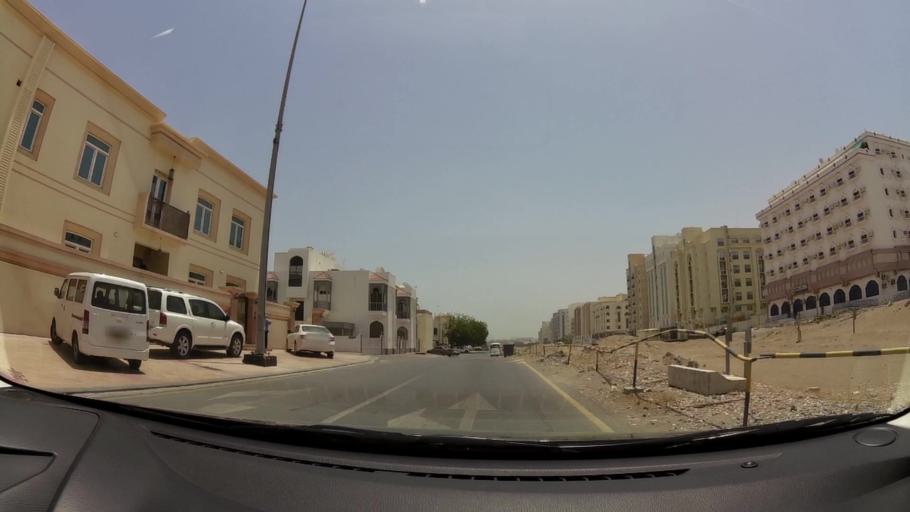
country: OM
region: Muhafazat Masqat
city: Bawshar
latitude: 23.5835
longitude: 58.4222
